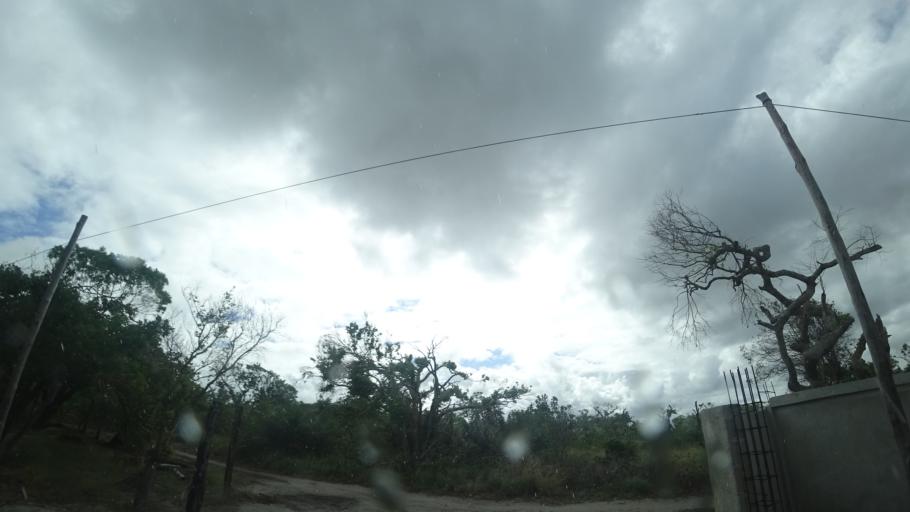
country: MZ
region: Sofala
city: Beira
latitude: -19.6122
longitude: 35.2203
